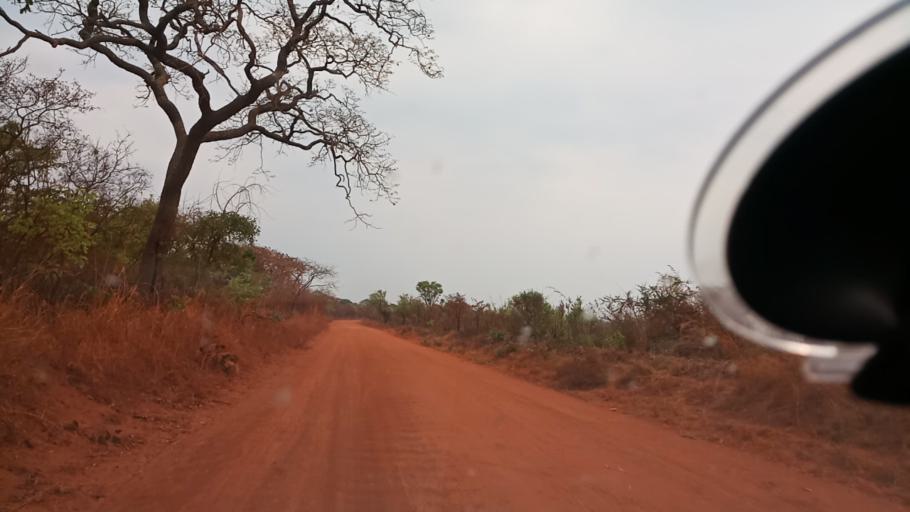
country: ZM
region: Luapula
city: Nchelenge
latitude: -9.1737
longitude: 28.2815
